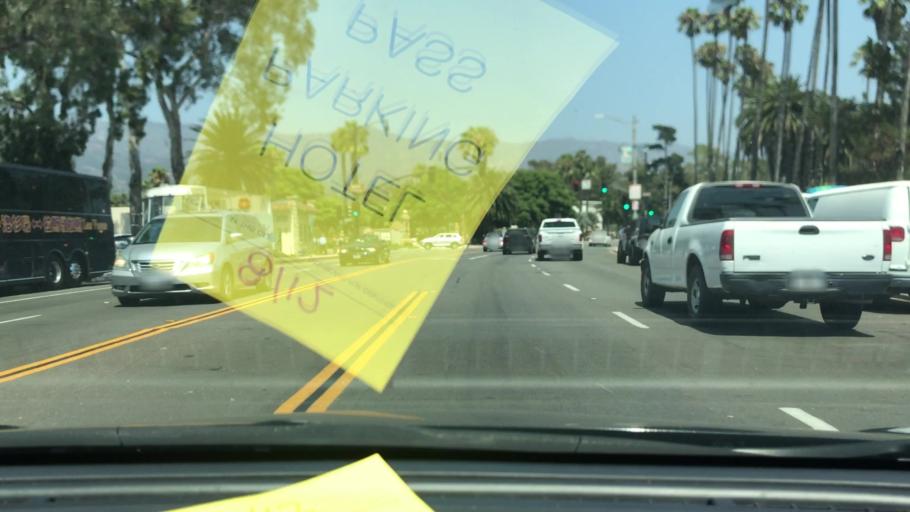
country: US
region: California
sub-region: Santa Barbara County
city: Santa Barbara
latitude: 34.4137
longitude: -119.6875
